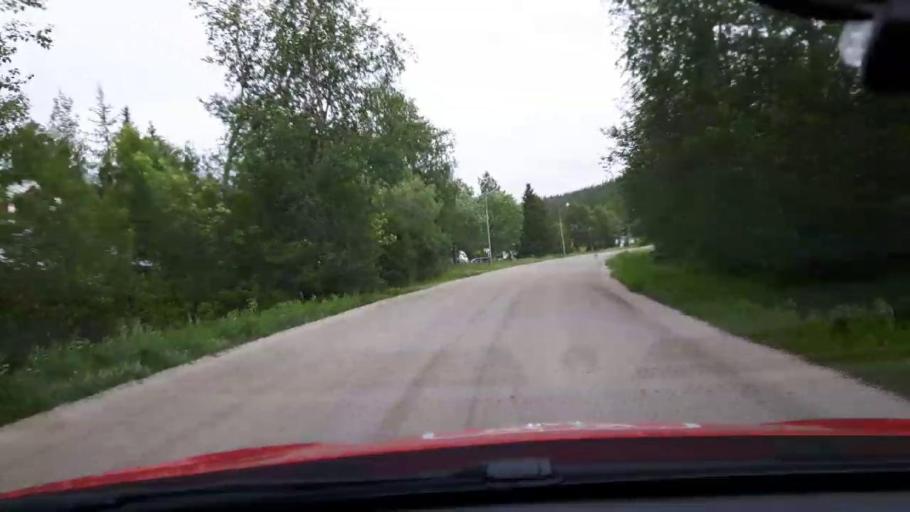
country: SE
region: Jaemtland
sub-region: Are Kommun
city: Are
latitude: 63.2568
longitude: 12.4518
